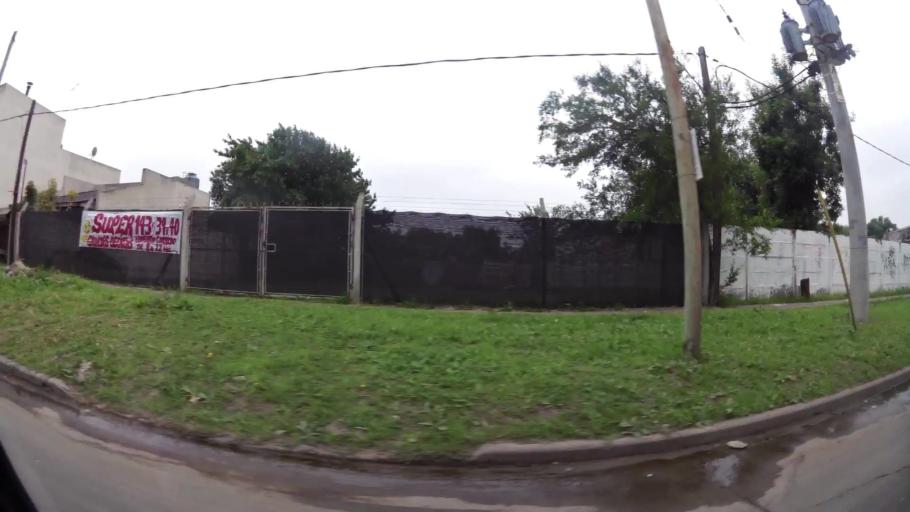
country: AR
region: Buenos Aires
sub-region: Partido de La Plata
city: La Plata
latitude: -34.9411
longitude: -57.9977
